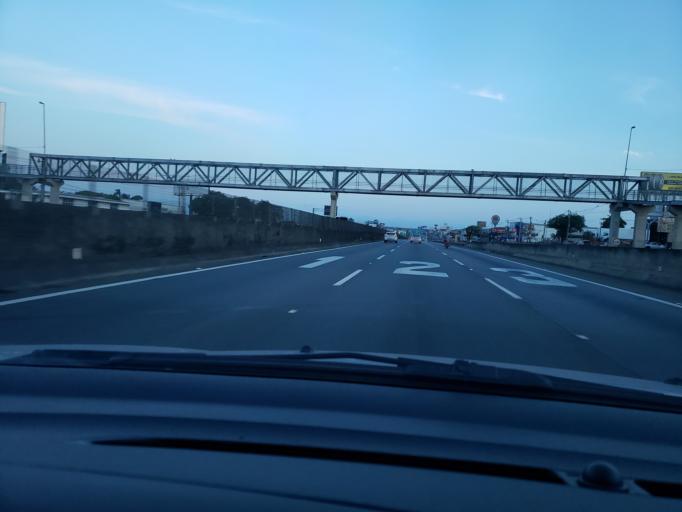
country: BR
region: Sao Paulo
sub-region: Hortolandia
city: Hortolandia
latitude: -22.8501
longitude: -47.1602
